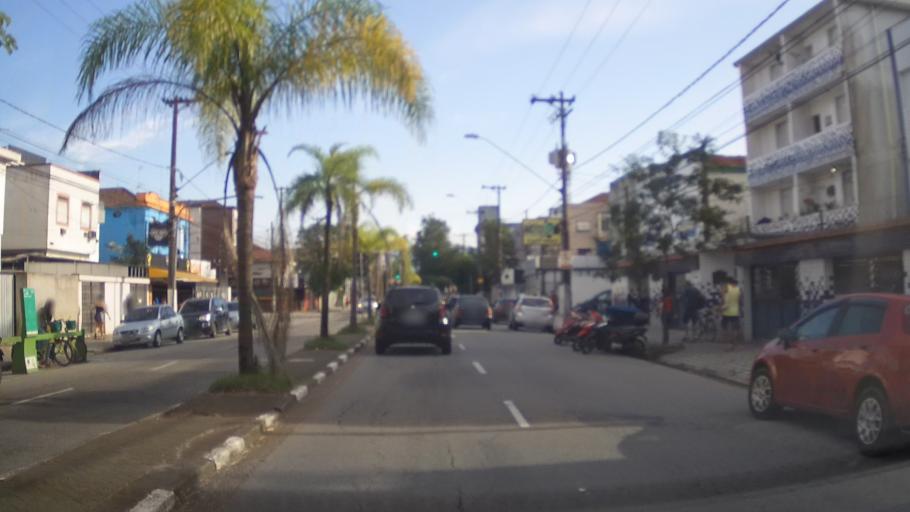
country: BR
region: Sao Paulo
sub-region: Santos
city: Santos
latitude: -23.9465
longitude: -46.3218
